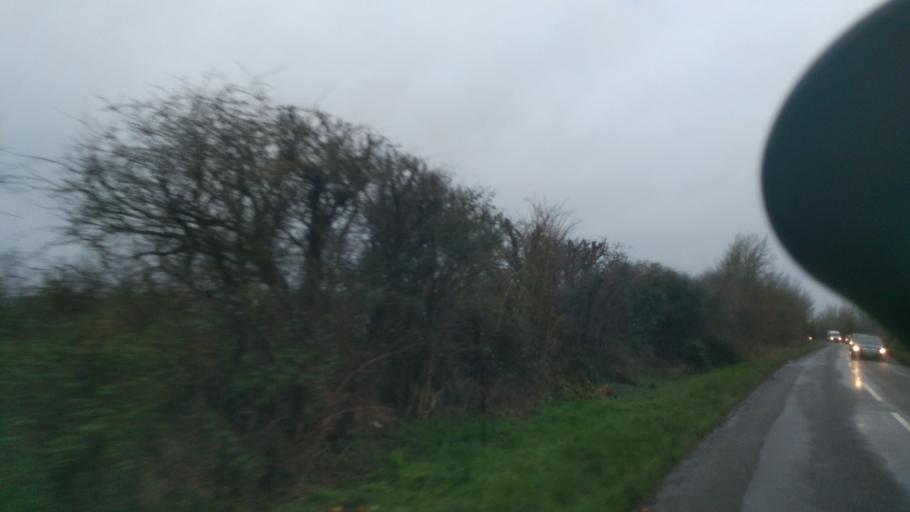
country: GB
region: England
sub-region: Oxfordshire
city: Shrivenham
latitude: 51.6150
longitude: -1.6518
